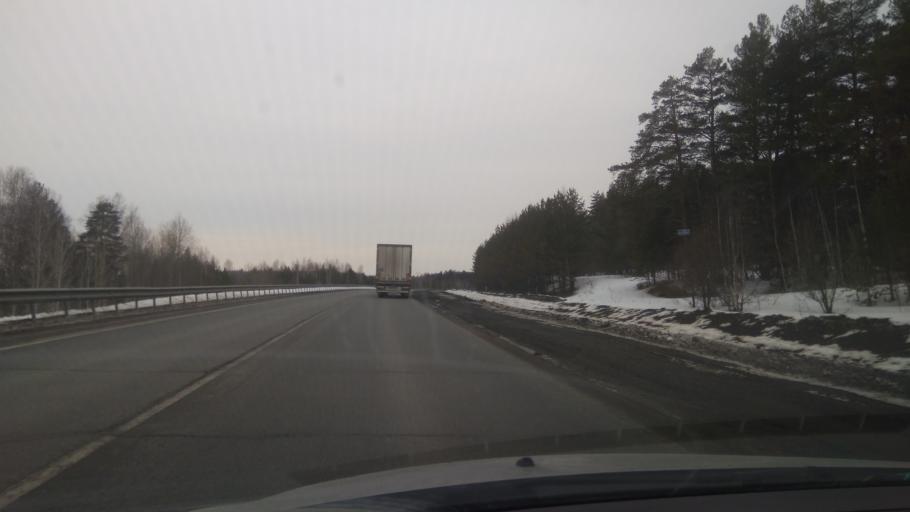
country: RU
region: Sverdlovsk
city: Ufimskiy
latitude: 56.7787
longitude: 58.2578
